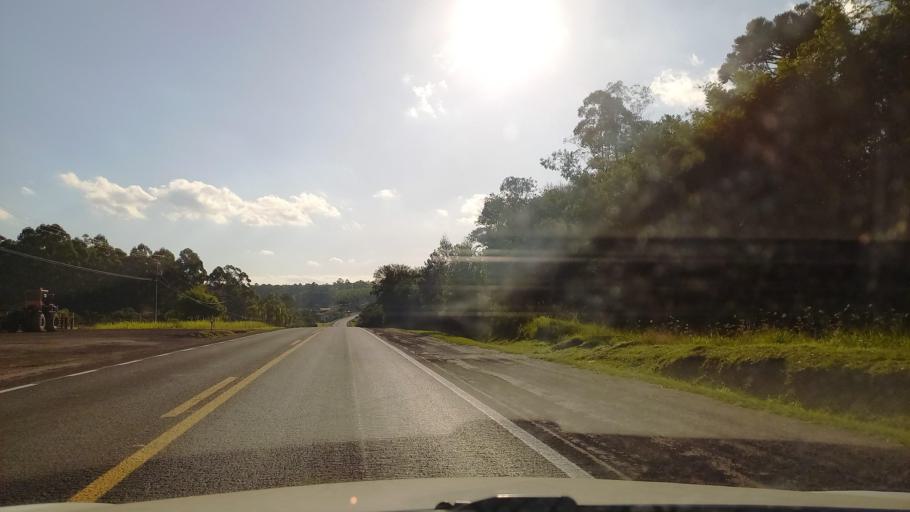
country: BR
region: Rio Grande do Sul
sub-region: Taquari
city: Taquari
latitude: -29.7099
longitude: -51.7808
